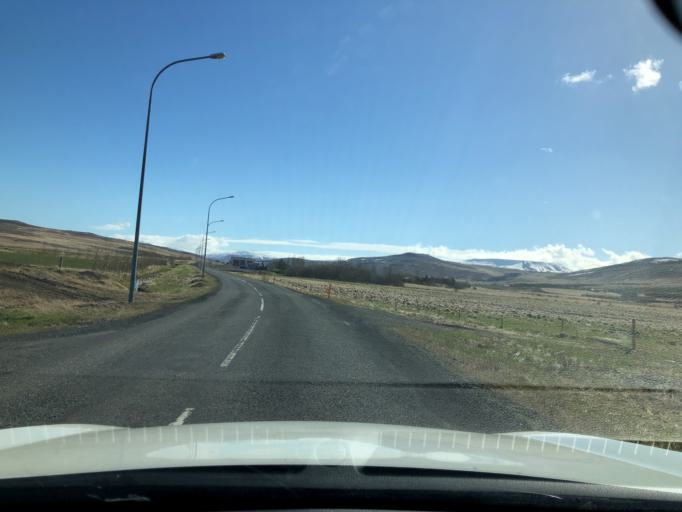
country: IS
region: West
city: Borgarnes
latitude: 64.6625
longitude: -21.2902
